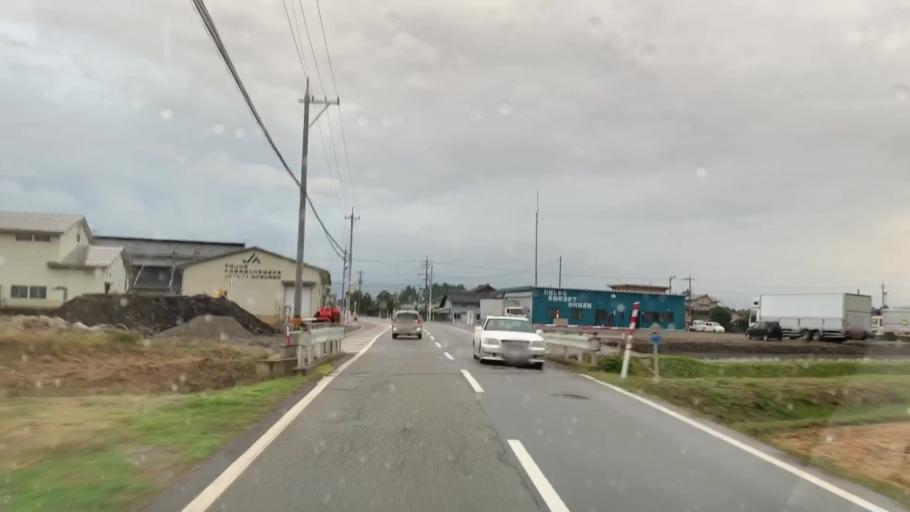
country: JP
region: Toyama
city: Kamiichi
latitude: 36.6481
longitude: 137.3280
